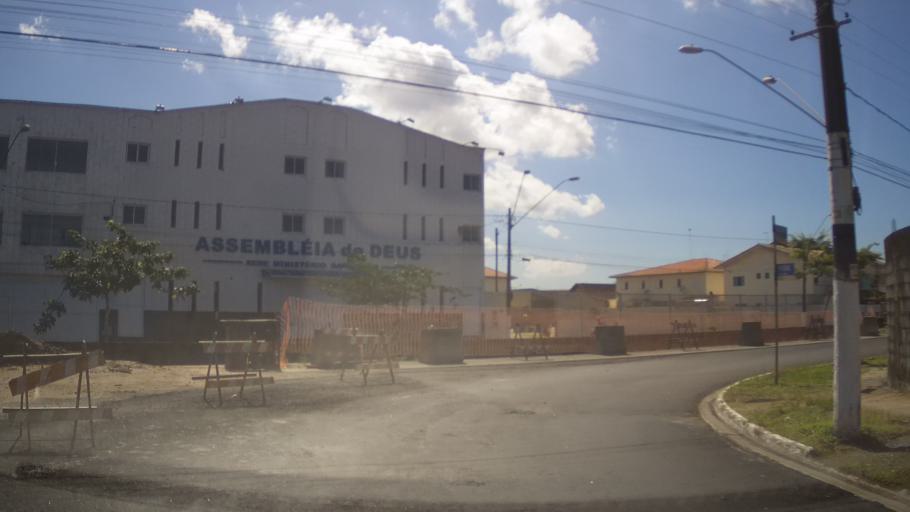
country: BR
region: Sao Paulo
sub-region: Mongagua
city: Mongagua
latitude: -24.0287
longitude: -46.5315
